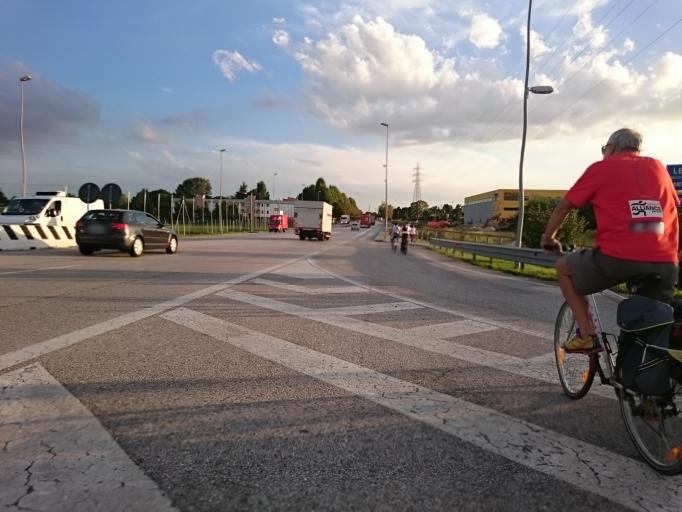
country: IT
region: Veneto
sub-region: Provincia di Padova
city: Ponte San Nicolo
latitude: 45.3812
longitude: 11.9385
